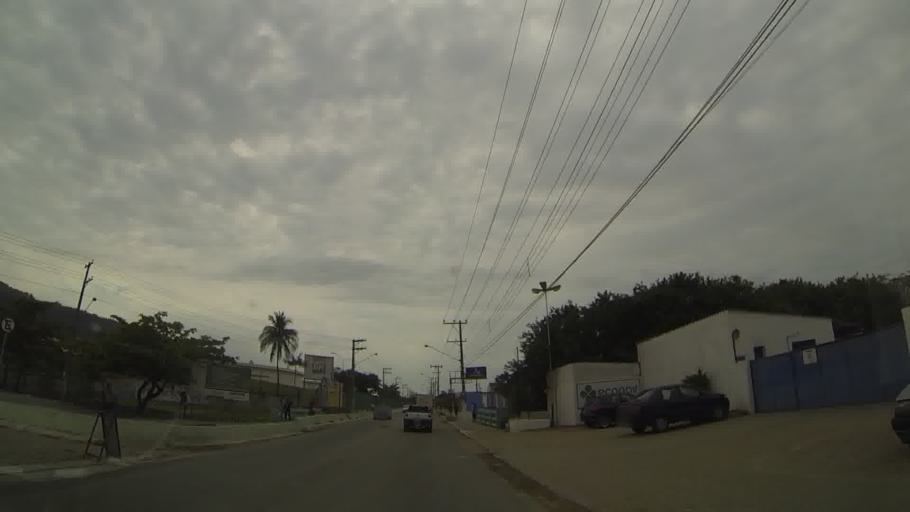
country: BR
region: Sao Paulo
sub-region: Sao Sebastiao
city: Sao Sebastiao
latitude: -23.8085
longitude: -45.4073
